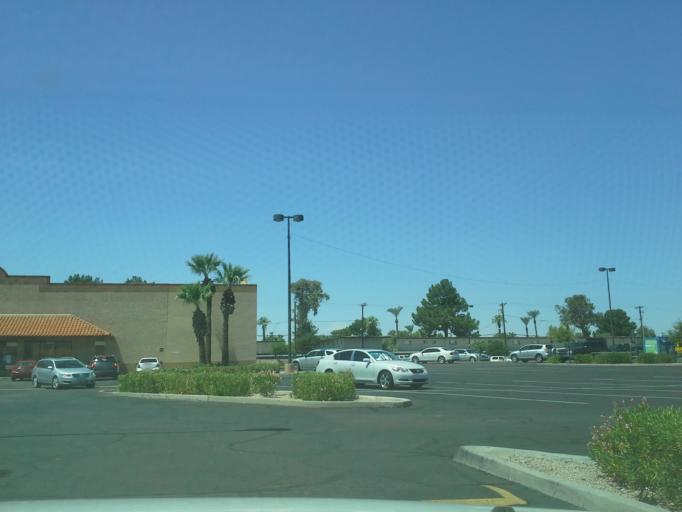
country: US
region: Arizona
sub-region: Maricopa County
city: Phoenix
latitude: 33.5101
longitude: -112.0849
